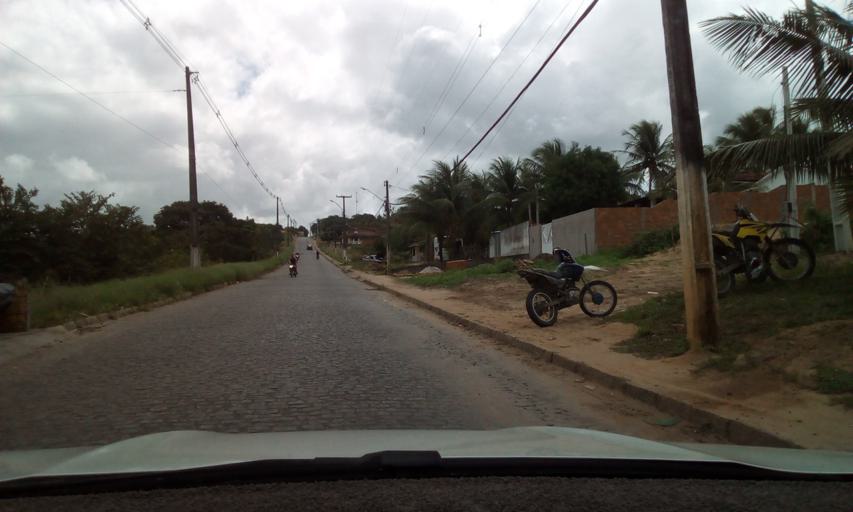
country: BR
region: Paraiba
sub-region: Rio Tinto
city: Rio Tinto
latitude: -6.7981
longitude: -35.0706
